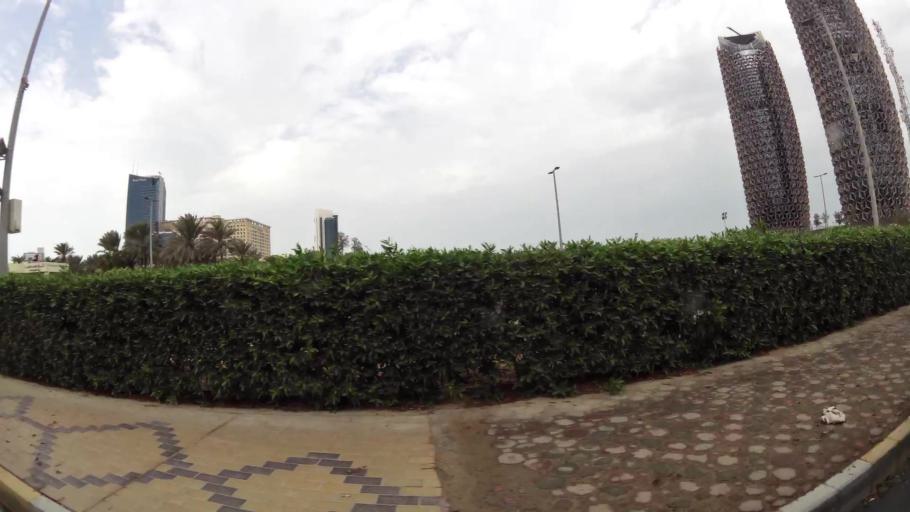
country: AE
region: Abu Dhabi
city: Abu Dhabi
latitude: 24.4540
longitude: 54.4006
